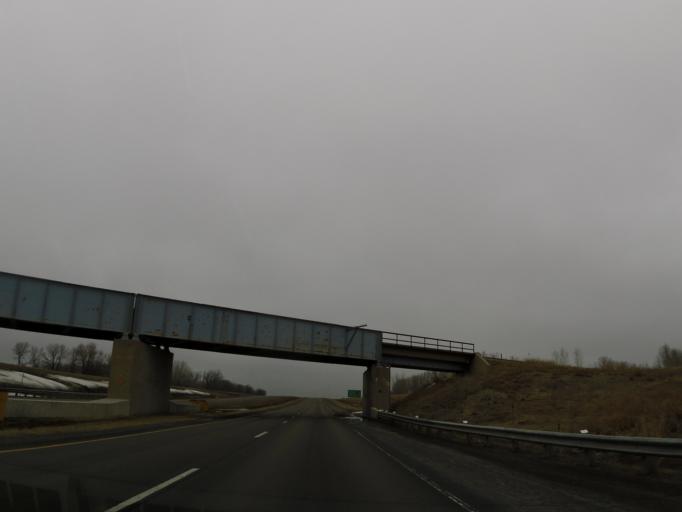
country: US
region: North Dakota
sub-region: Walsh County
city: Grafton
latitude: 48.5309
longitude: -97.1857
